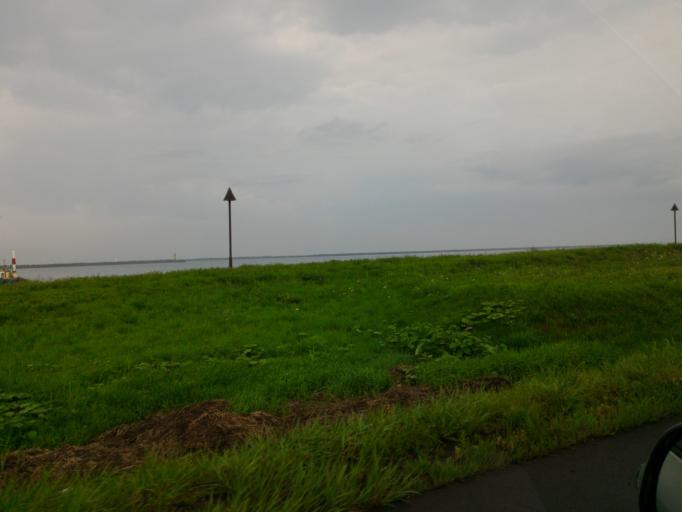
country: JP
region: Hokkaido
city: Rumoi
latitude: 43.9613
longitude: 141.6429
